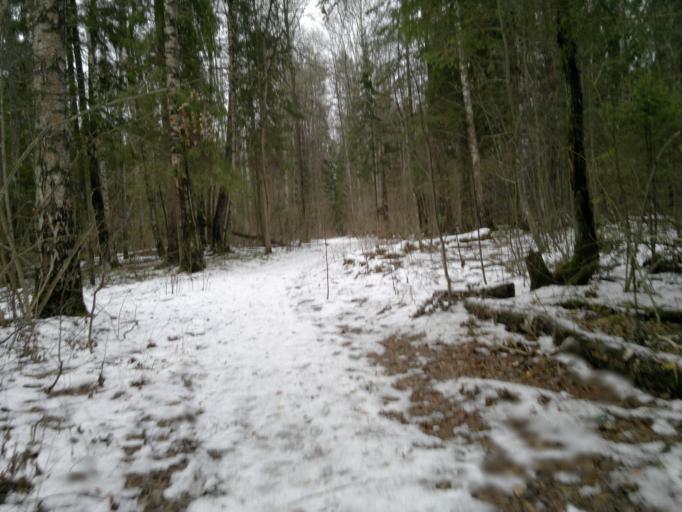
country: RU
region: Mariy-El
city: Yoshkar-Ola
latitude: 56.6115
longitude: 47.9411
